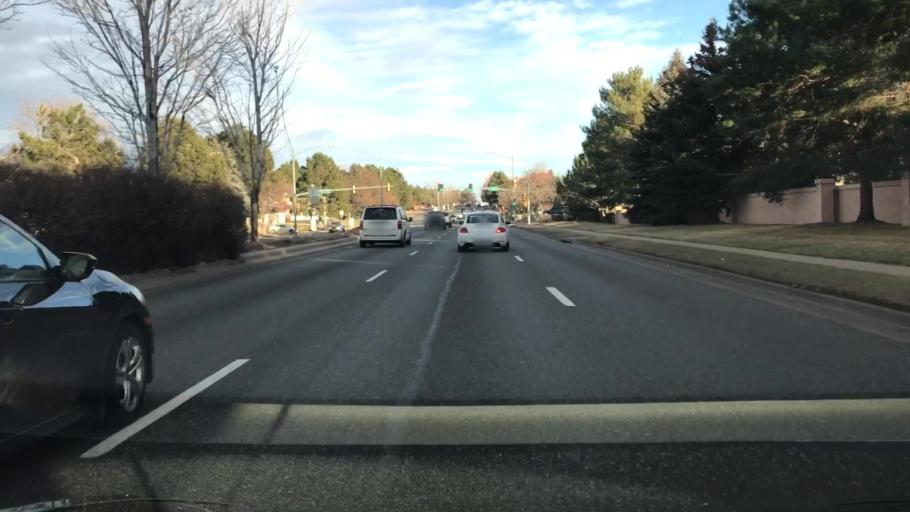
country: US
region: Colorado
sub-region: Adams County
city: Aurora
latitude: 39.6749
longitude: -104.8440
